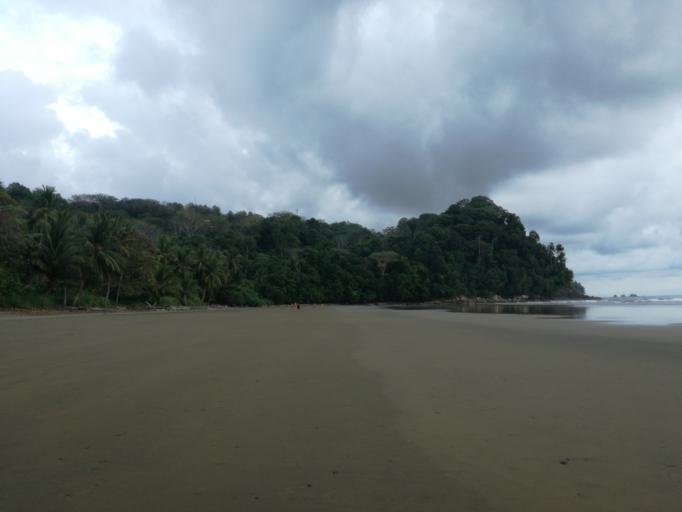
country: CR
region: San Jose
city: Mercedes
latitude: 9.1470
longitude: -83.7304
